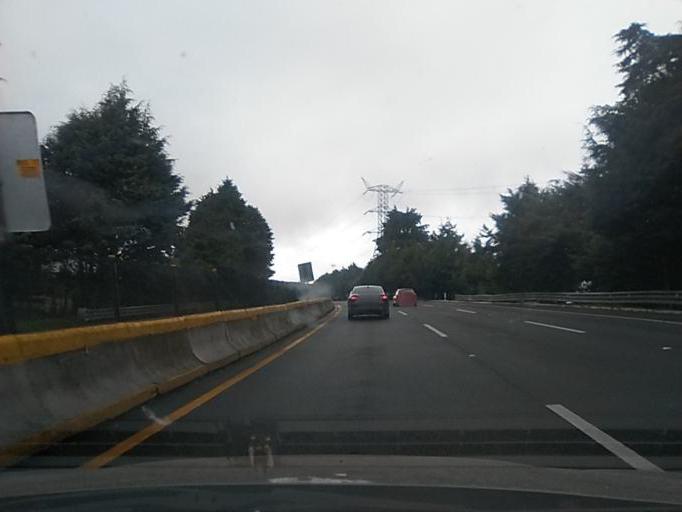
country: MX
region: Morelos
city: Tres Marias
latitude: 19.1326
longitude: -99.1706
